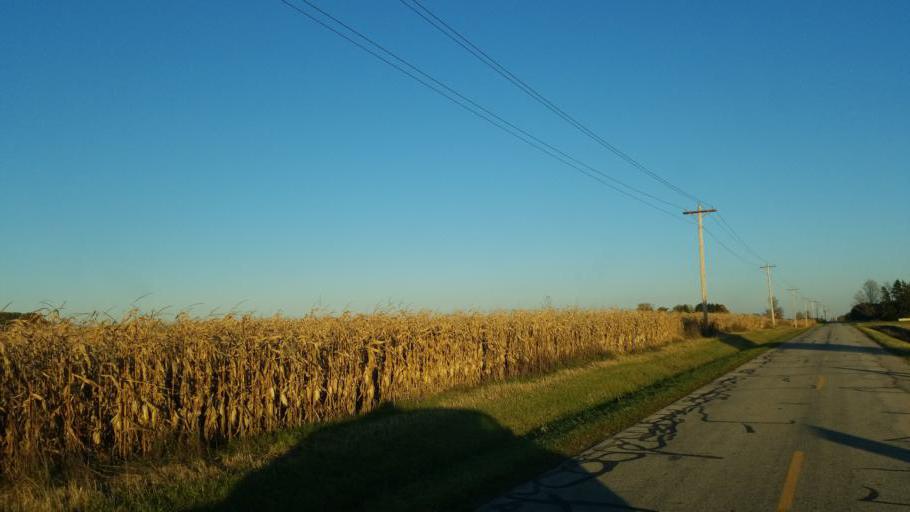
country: US
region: Ohio
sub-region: Sandusky County
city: Mount Carmel
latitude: 41.2125
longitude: -82.9709
